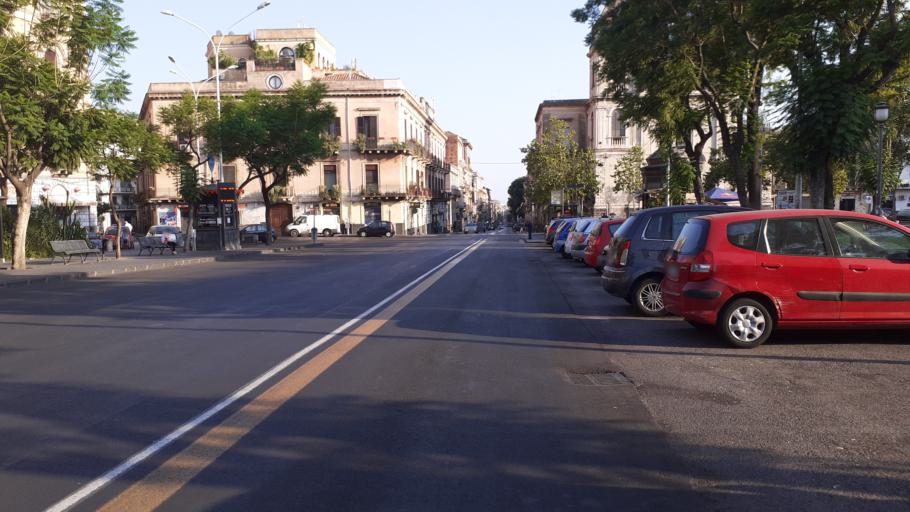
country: IT
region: Sicily
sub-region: Catania
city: Canalicchio
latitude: 37.5177
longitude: 15.0837
